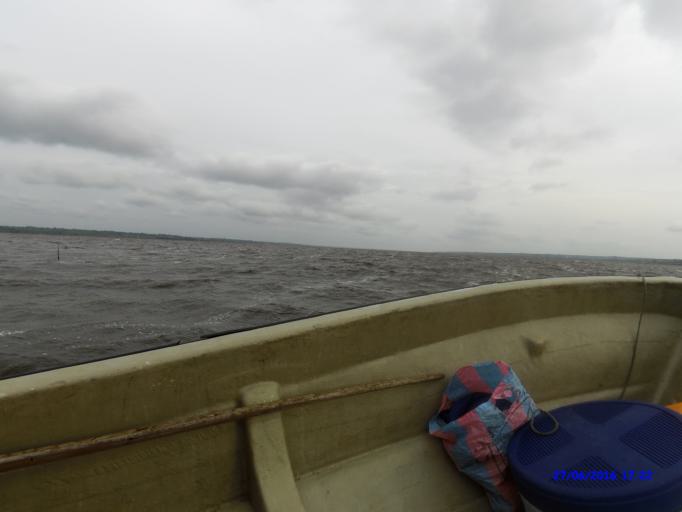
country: BJ
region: Atlantique
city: Allada
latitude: 6.6025
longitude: 1.9815
